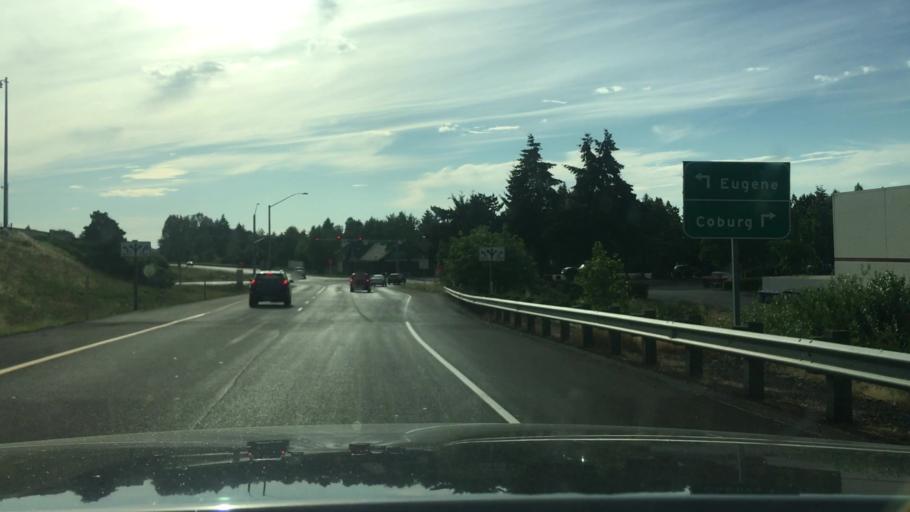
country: US
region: Oregon
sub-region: Lane County
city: Eugene
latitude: 44.0879
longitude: -123.0661
